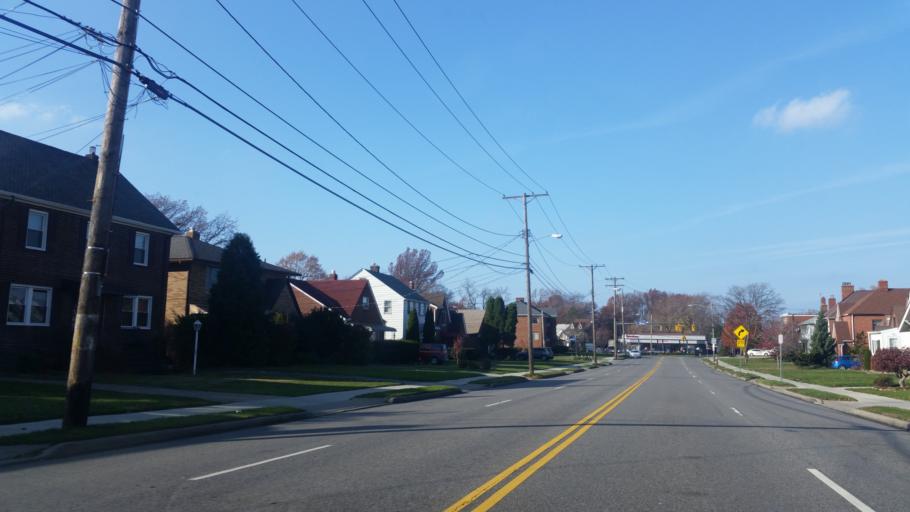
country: US
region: Ohio
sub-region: Cuyahoga County
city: Lakewood
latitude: 41.4574
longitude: -81.8037
